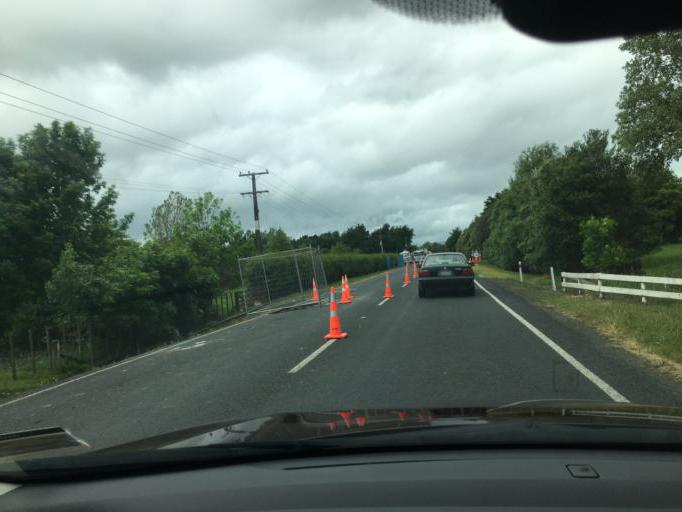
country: NZ
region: Waikato
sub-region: Waipa District
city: Cambridge
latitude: -37.9177
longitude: 175.4416
